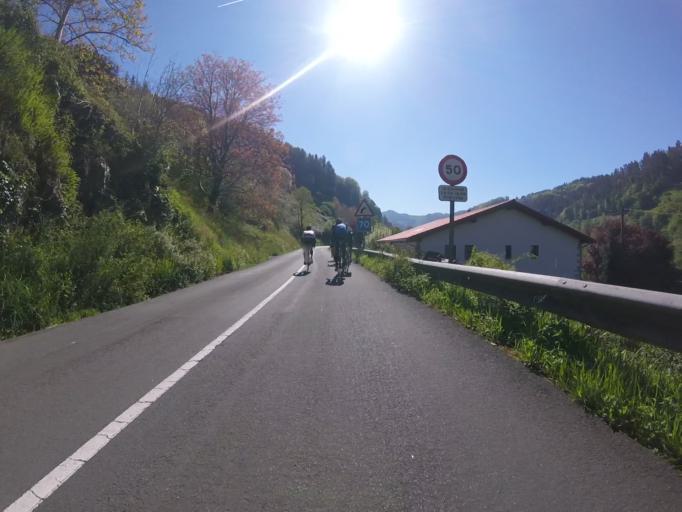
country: ES
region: Basque Country
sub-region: Provincia de Guipuzcoa
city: Errezil
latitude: 43.1709
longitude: -2.1977
